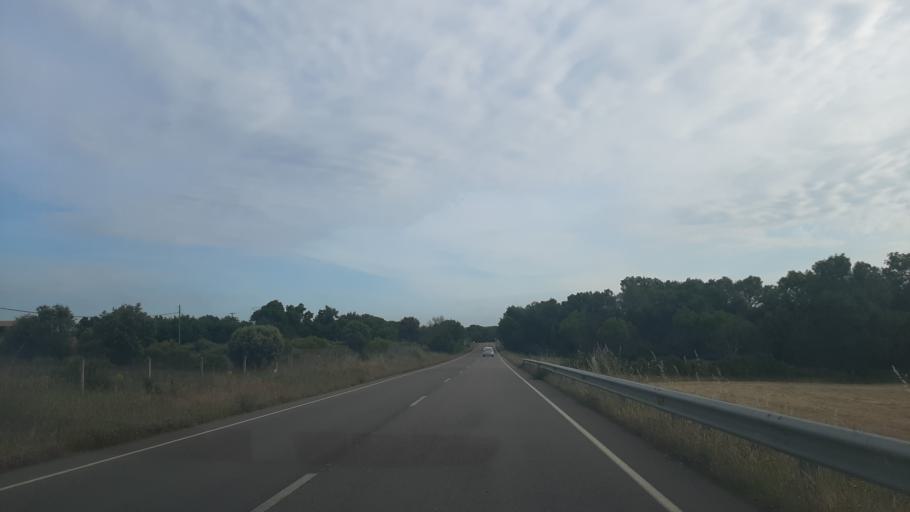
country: ES
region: Castille and Leon
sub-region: Provincia de Salamanca
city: Gallegos de Arganan
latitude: 40.6018
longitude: -6.7043
